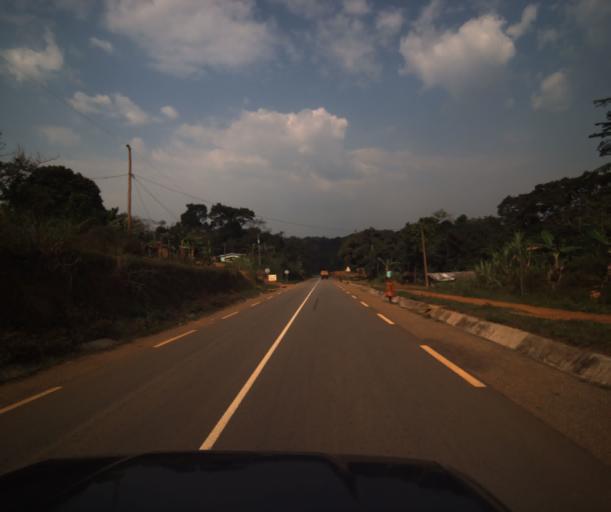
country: CM
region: Centre
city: Mbankomo
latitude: 3.6538
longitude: 11.3378
